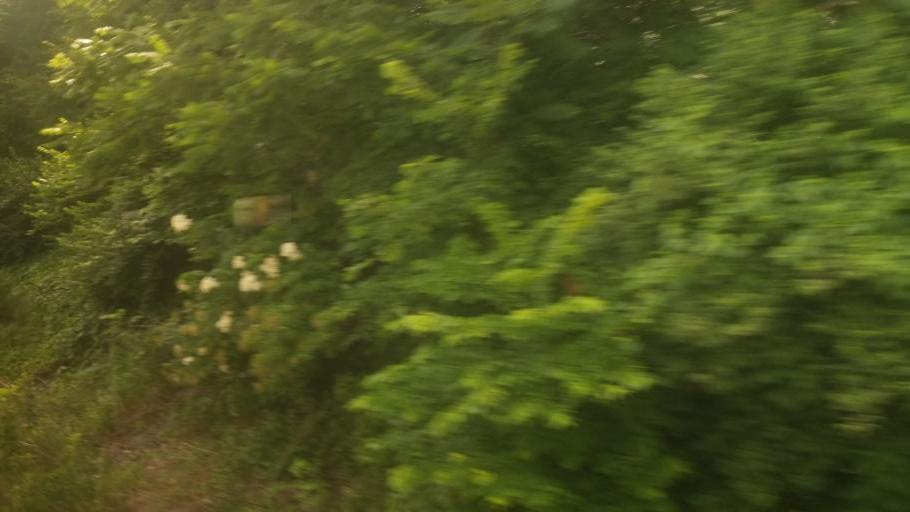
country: US
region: Missouri
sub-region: Jackson County
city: Sugar Creek
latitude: 39.1218
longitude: -94.4545
